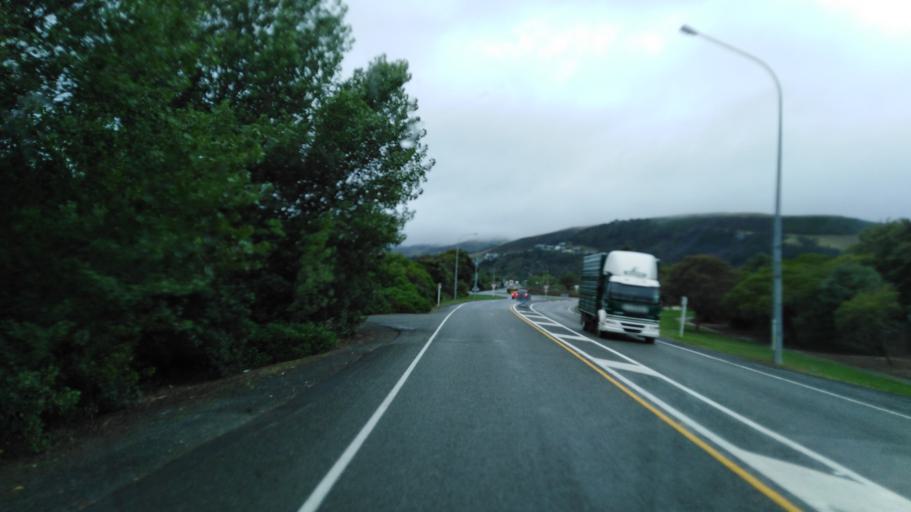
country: NZ
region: Nelson
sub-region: Nelson City
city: Nelson
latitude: -41.2655
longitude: 173.2820
